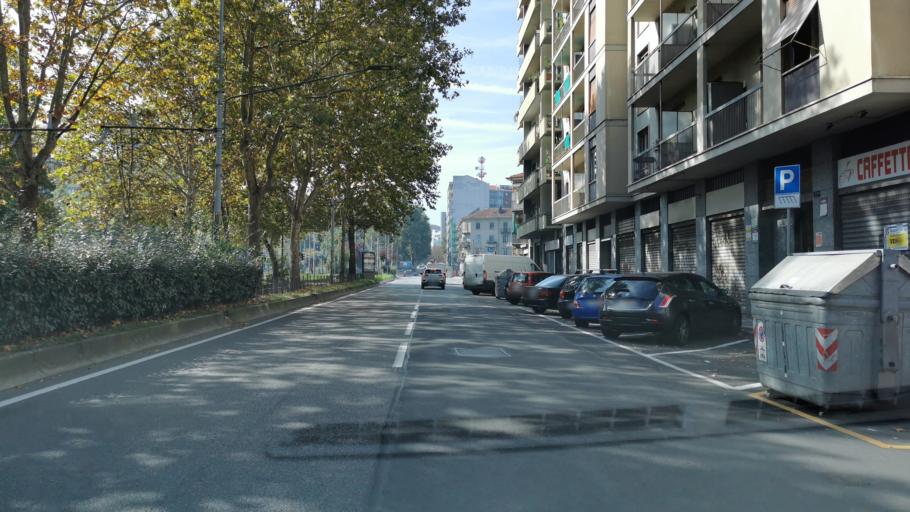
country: IT
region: Piedmont
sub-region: Provincia di Torino
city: Turin
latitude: 45.0883
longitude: 7.6578
